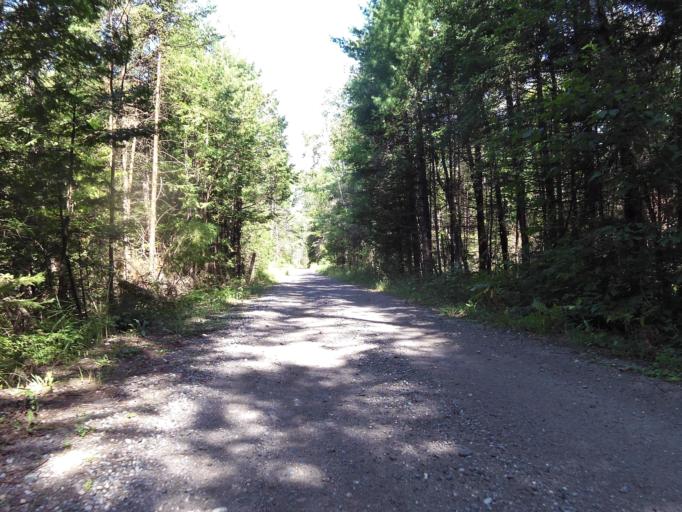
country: CA
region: Ontario
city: Renfrew
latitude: 45.0865
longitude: -76.7208
